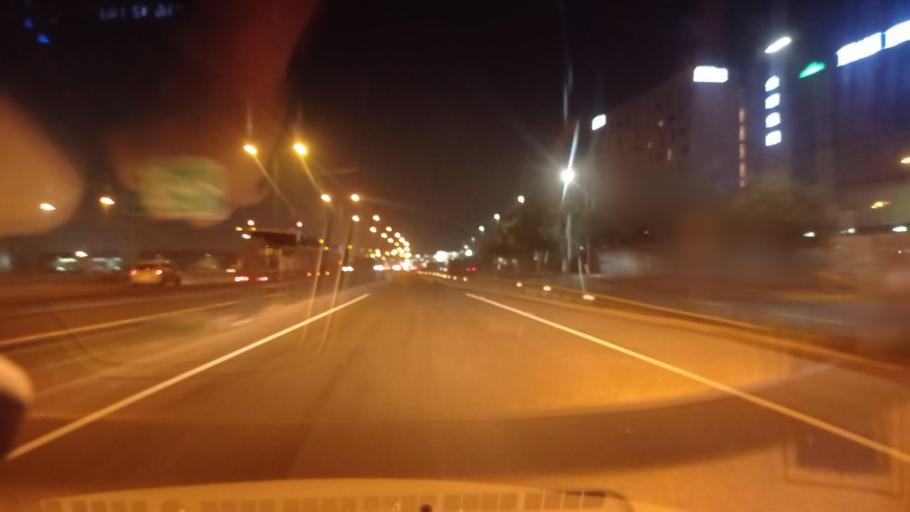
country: CL
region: Santiago Metropolitan
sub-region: Provincia de Santiago
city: Lo Prado
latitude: -33.4278
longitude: -70.7844
